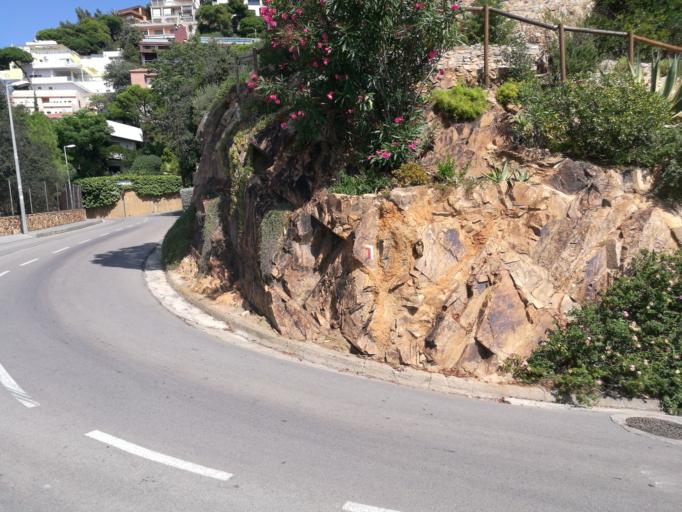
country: ES
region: Catalonia
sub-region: Provincia de Girona
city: Blanes
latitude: 41.6771
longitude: 2.7962
